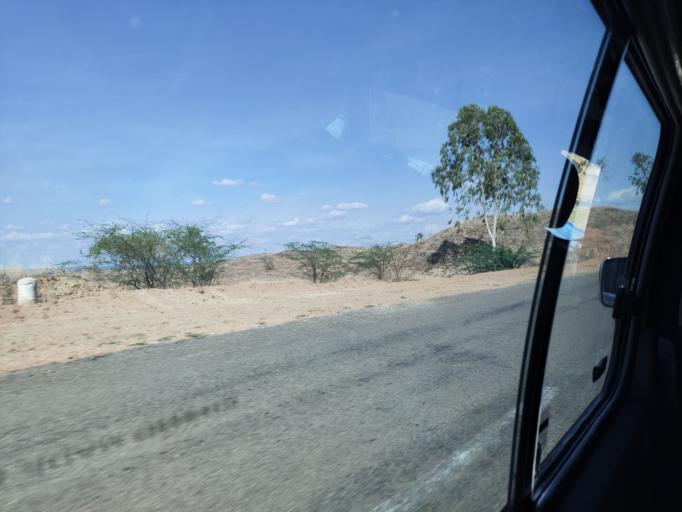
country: MM
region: Magway
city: Yenangyaung
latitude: 20.4725
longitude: 94.9194
